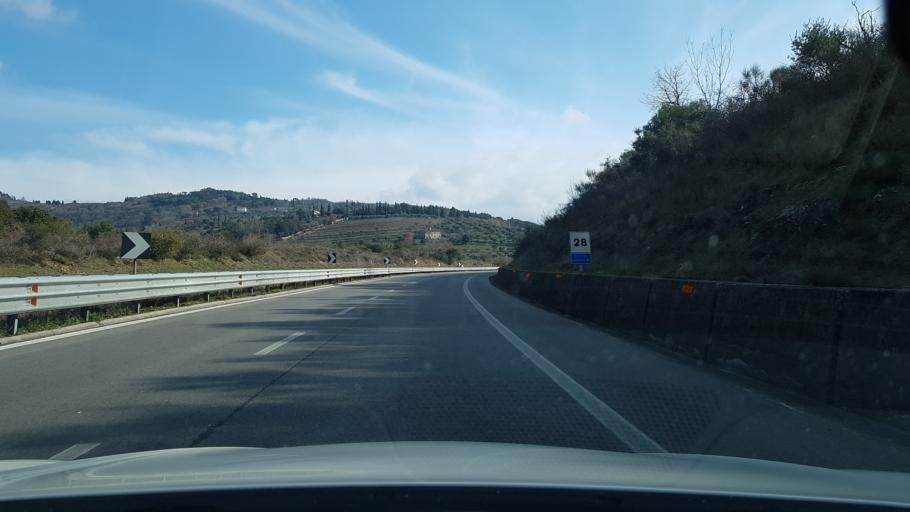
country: IT
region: Umbria
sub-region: Provincia di Perugia
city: Passignano sul Trasimeno
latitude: 43.1970
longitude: 12.1264
